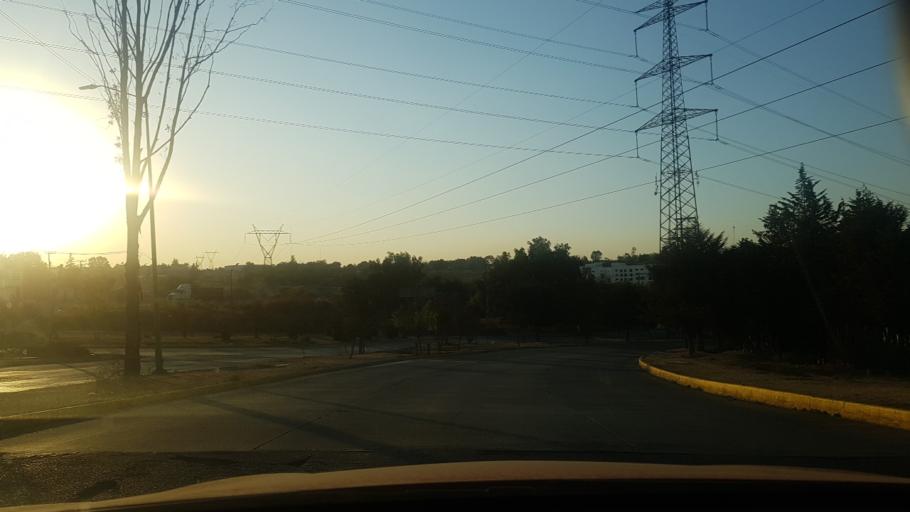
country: MX
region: Mexico
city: Cuautitlan Izcalli
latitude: 19.6357
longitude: -99.2186
